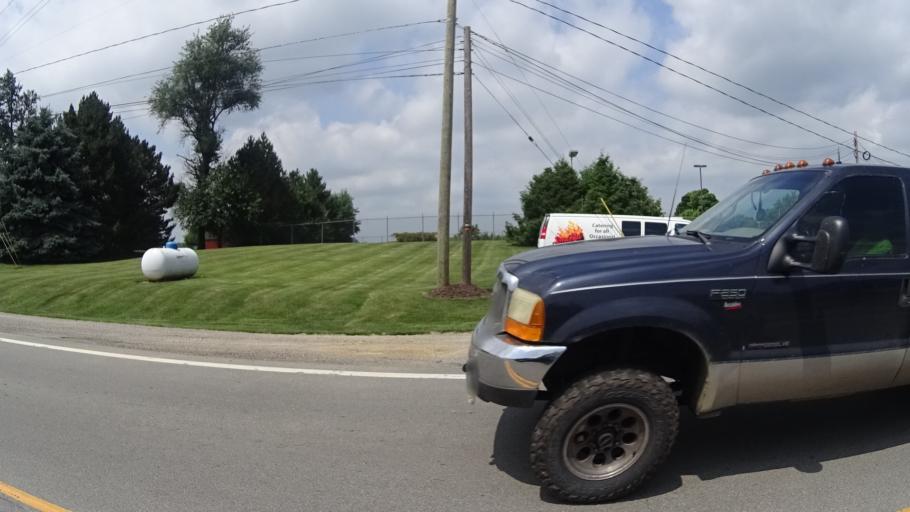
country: US
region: Ohio
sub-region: Lorain County
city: Vermilion
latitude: 41.3684
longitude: -82.3634
